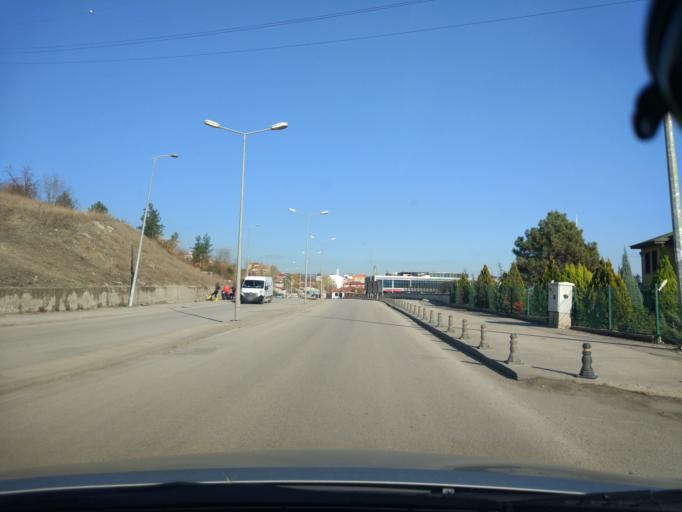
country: TR
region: Karabuk
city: Karabuk
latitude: 41.2045
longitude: 32.6318
